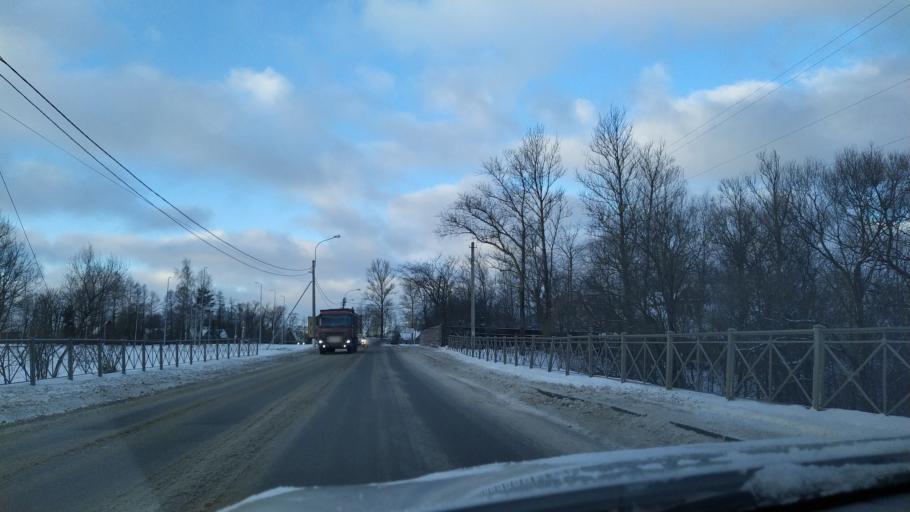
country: RU
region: St.-Petersburg
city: Aleksandrovskaya
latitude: 59.7291
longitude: 30.3586
